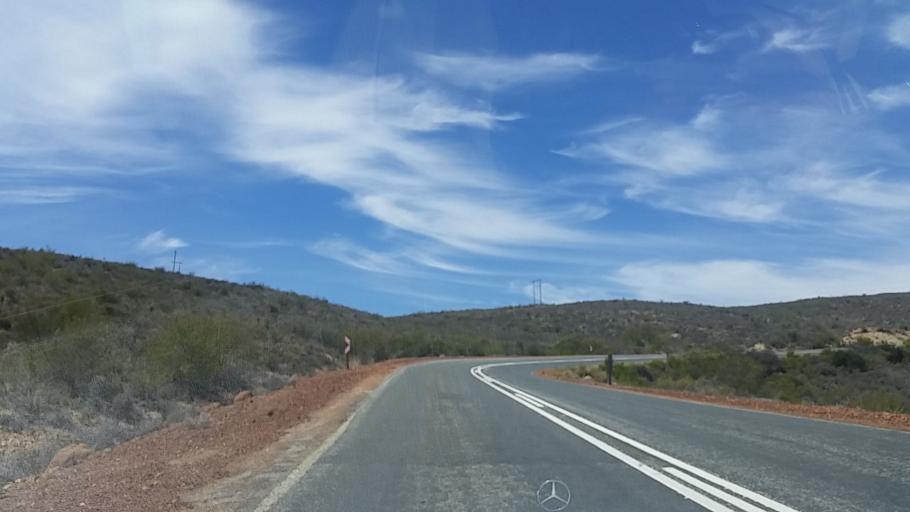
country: ZA
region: Western Cape
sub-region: Eden District Municipality
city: Knysna
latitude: -33.6971
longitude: 23.0444
